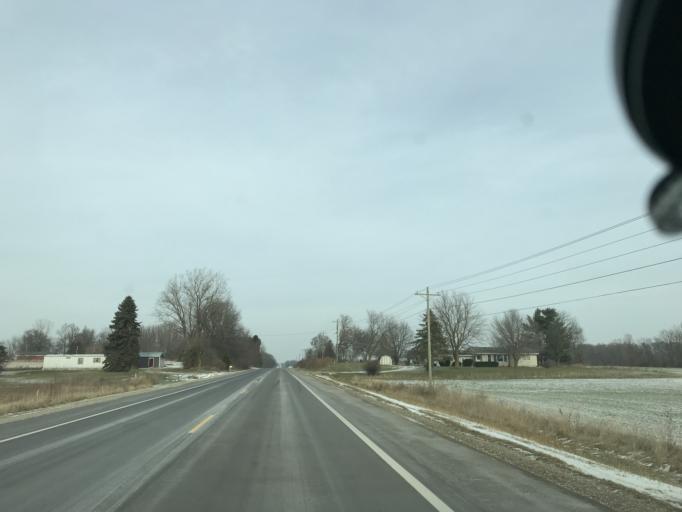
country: US
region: Michigan
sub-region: Ionia County
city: Lake Odessa
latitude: 42.7893
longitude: -85.0744
